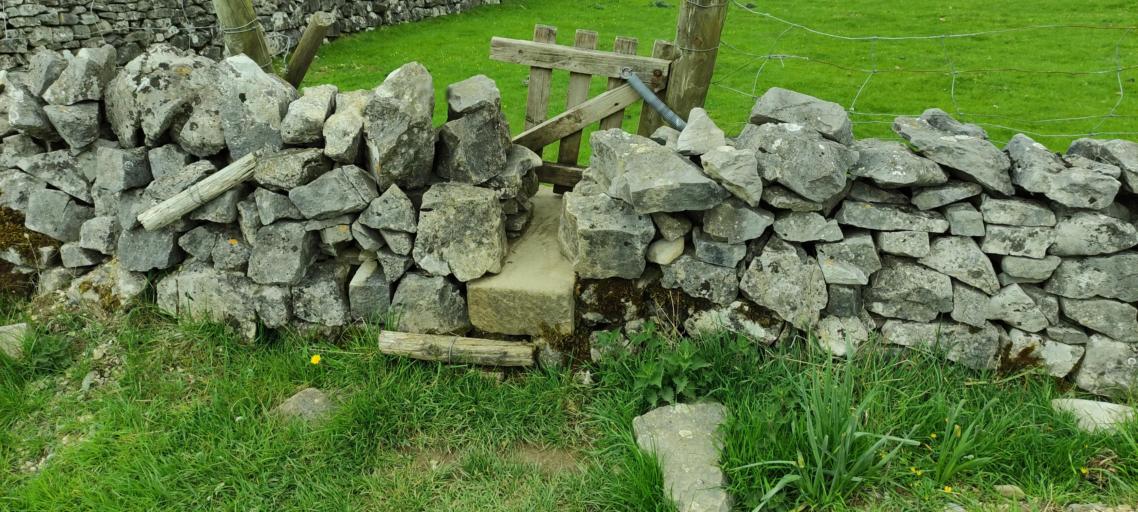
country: GB
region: England
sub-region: North Yorkshire
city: Ingleton
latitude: 54.1553
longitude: -2.4454
